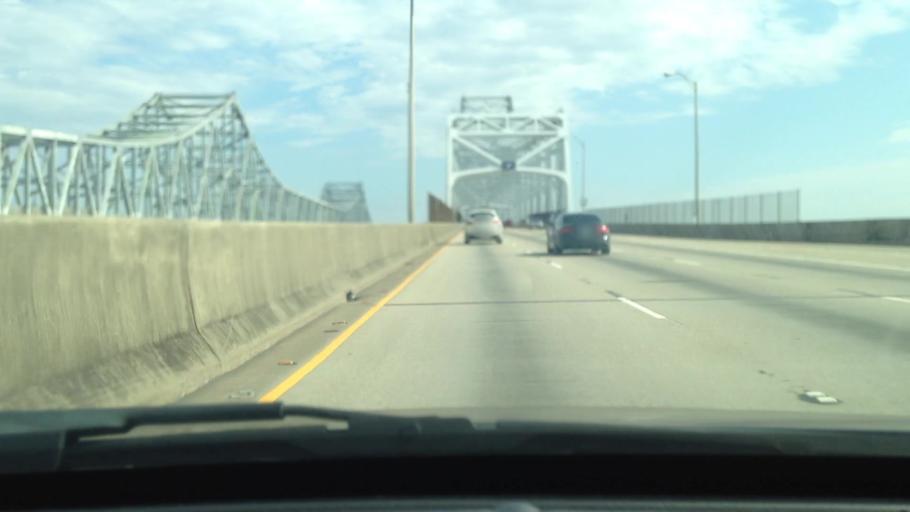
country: US
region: Louisiana
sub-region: Orleans Parish
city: New Orleans
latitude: 29.9378
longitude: -90.0630
